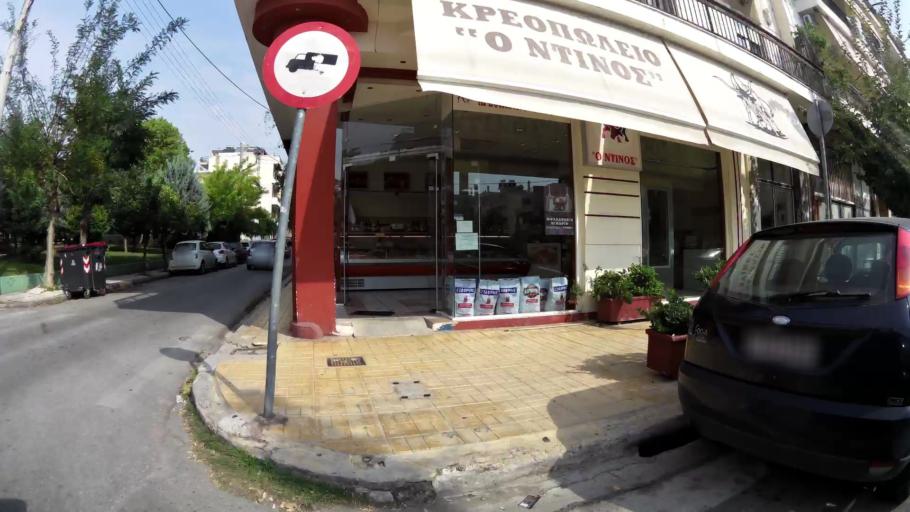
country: GR
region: Attica
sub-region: Nomarchia Athinas
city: Peristeri
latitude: 38.0170
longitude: 23.6800
